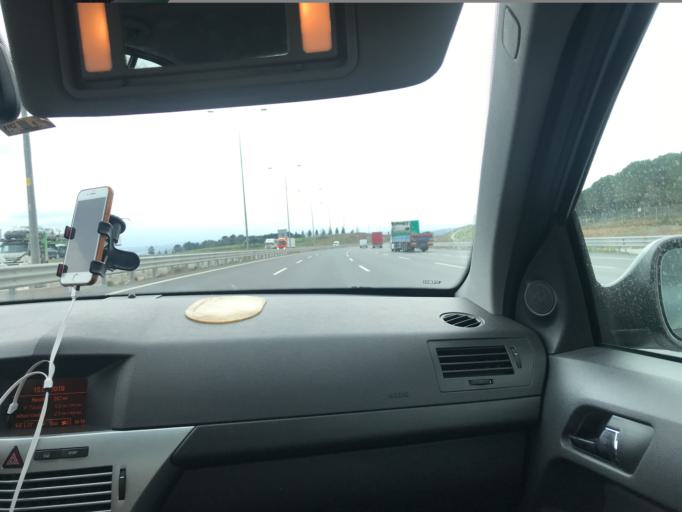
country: TR
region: Istanbul
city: Sultanbeyli
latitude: 40.9906
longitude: 29.3264
